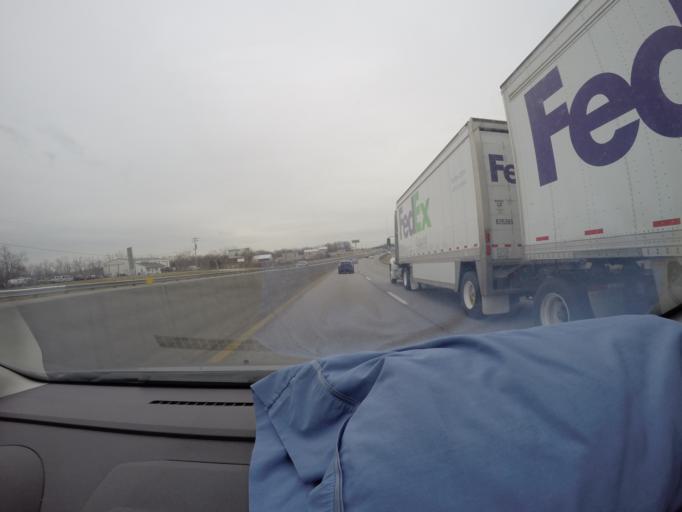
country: US
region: Missouri
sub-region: Warren County
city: Wright City
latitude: 38.8297
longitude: -91.0141
